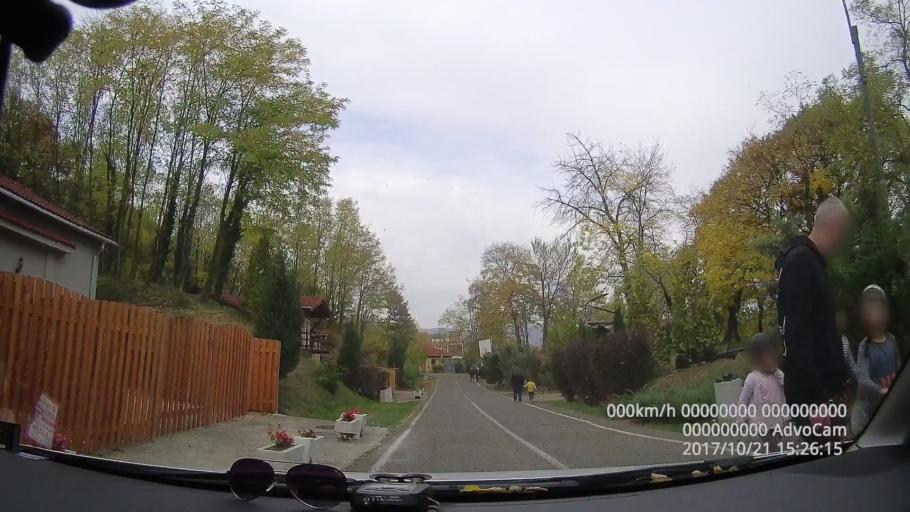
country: RO
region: Hunedoara
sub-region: Municipiul Deva
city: Deva
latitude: 45.8671
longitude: 22.9224
